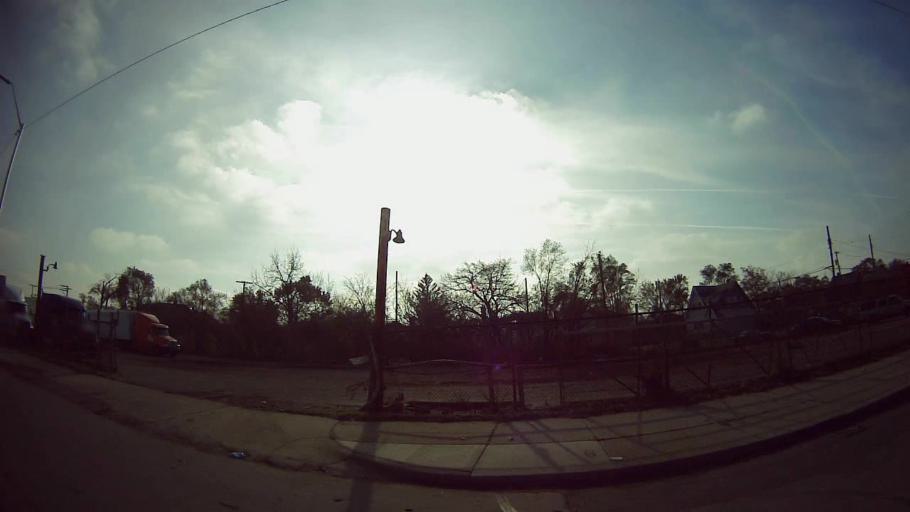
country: US
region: Michigan
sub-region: Wayne County
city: Dearborn
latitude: 42.3828
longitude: -83.1741
